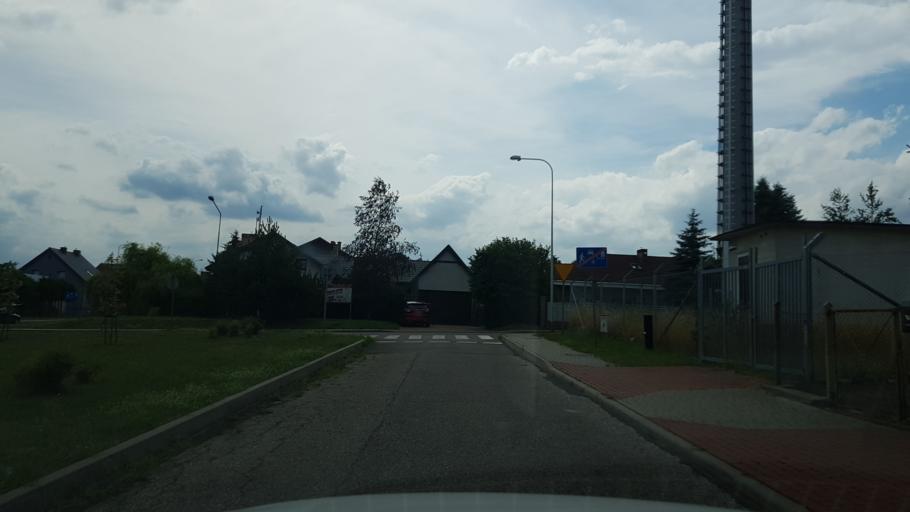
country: PL
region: West Pomeranian Voivodeship
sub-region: Powiat drawski
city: Drawsko Pomorskie
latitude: 53.5422
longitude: 15.8064
